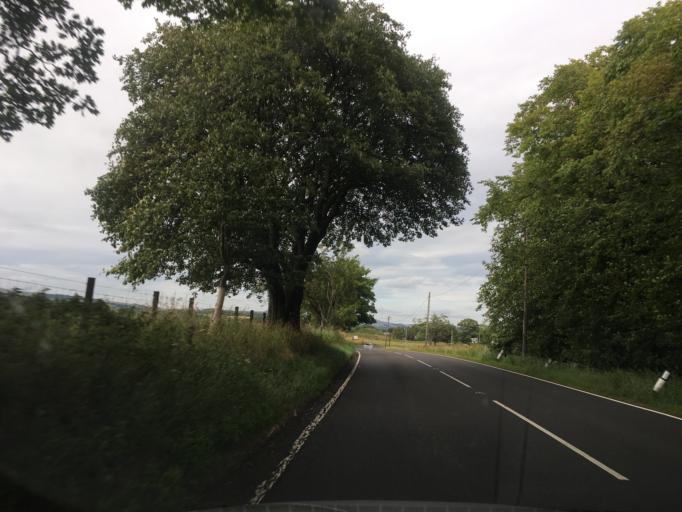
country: GB
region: Scotland
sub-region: South Lanarkshire
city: Biggar
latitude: 55.5825
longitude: -3.5647
